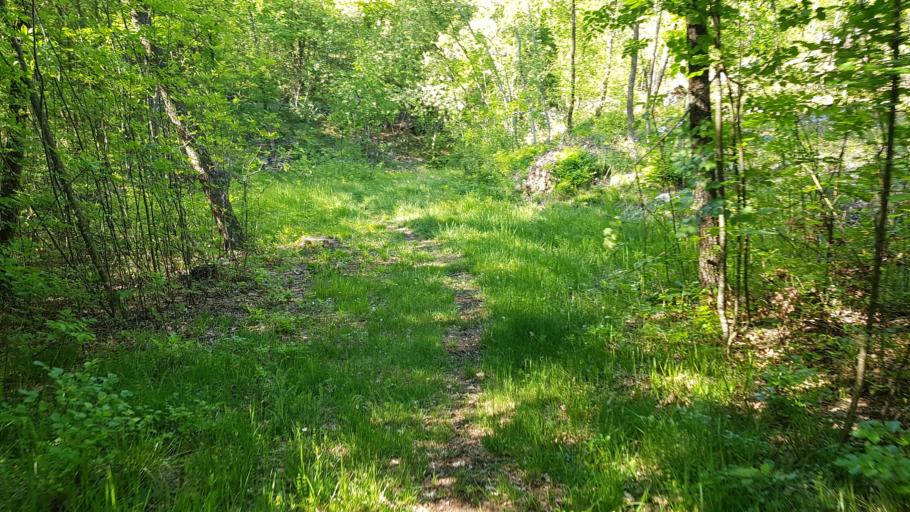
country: IT
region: Trentino-Alto Adige
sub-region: Provincia di Trento
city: Vezzano
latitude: 46.0898
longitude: 11.0001
